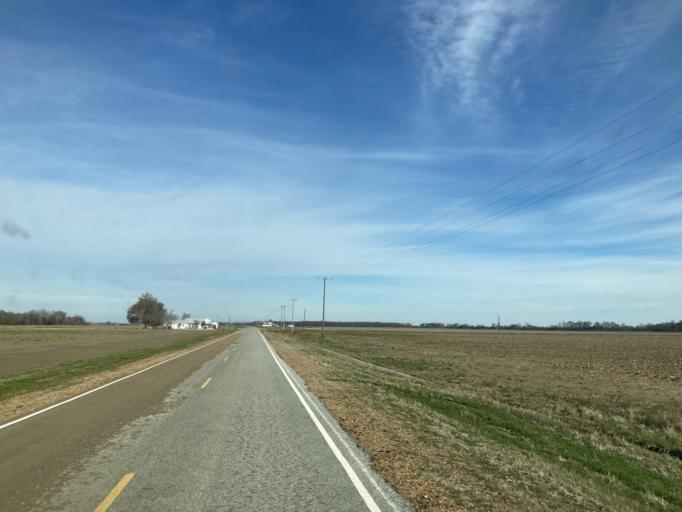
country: US
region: Mississippi
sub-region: Humphreys County
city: Belzoni
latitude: 33.0209
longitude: -90.6230
